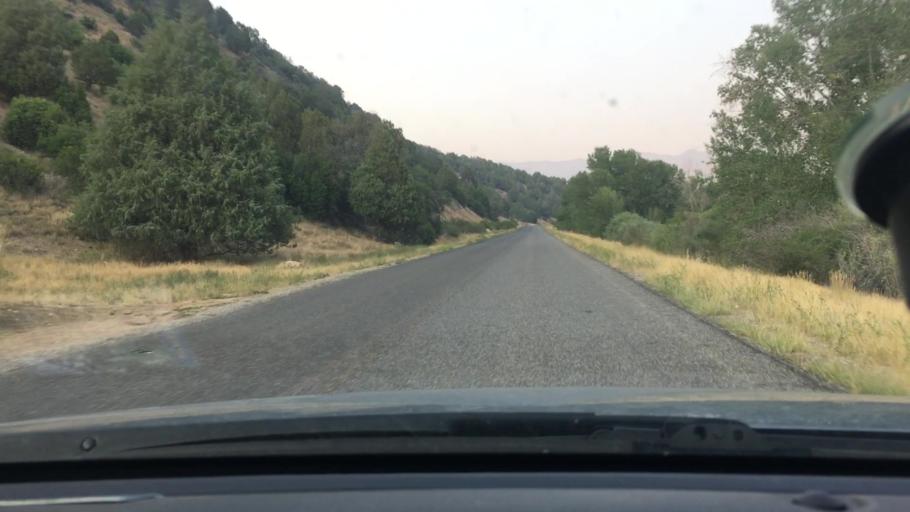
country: US
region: Utah
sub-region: Utah County
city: Mapleton
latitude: 40.0541
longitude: -111.4617
